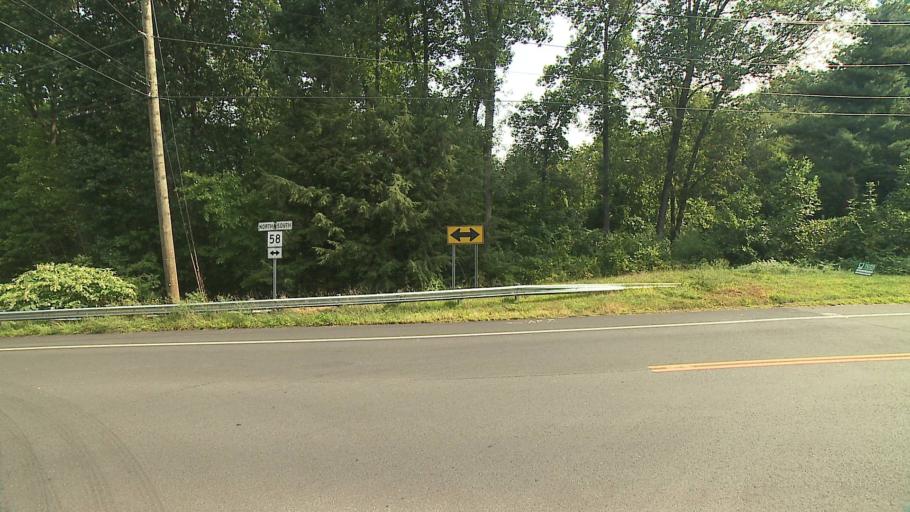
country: US
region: Connecticut
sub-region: Fairfield County
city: Bethel
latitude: 41.3385
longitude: -73.3808
